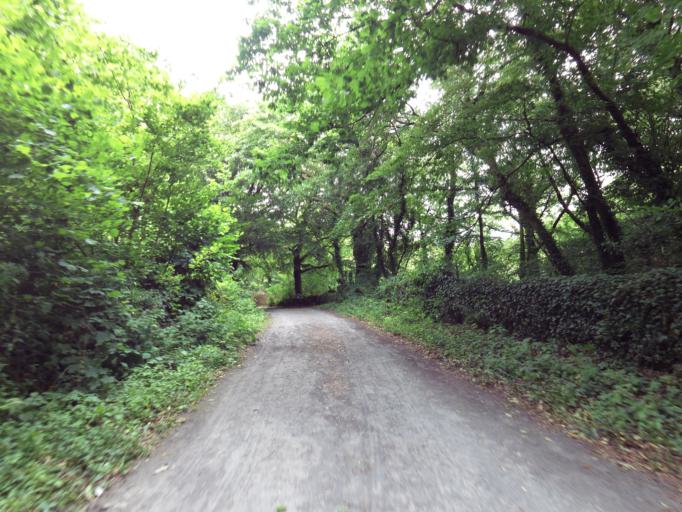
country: IE
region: Connaught
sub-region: County Galway
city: Gort
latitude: 53.0798
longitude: -8.8789
